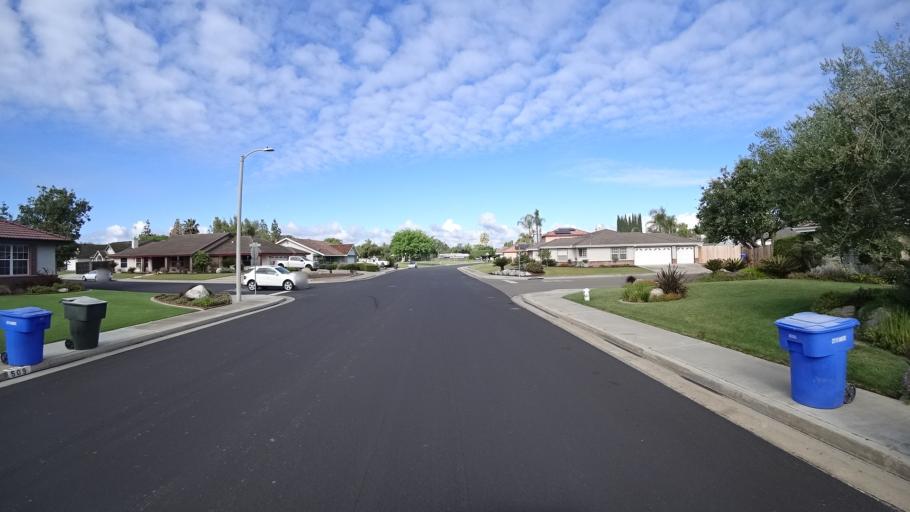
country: US
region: California
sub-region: Kings County
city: Lucerne
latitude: 36.3621
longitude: -119.6396
